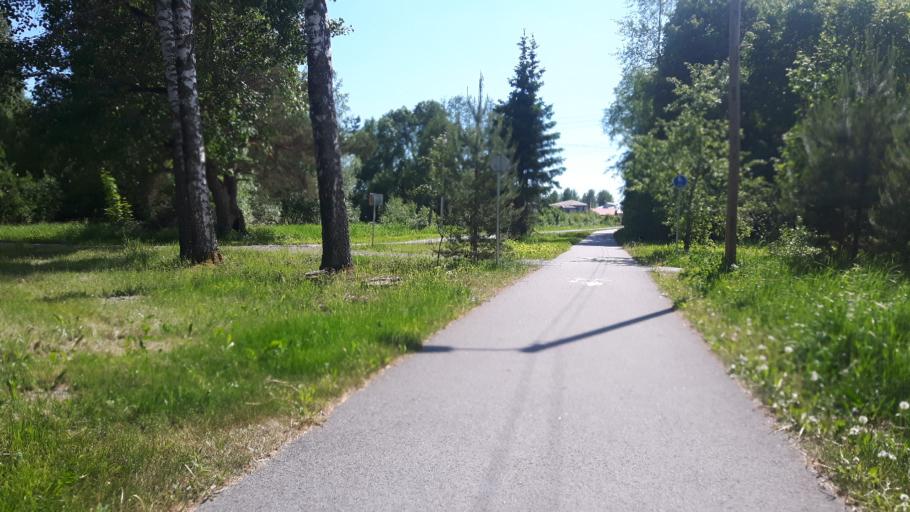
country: EE
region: Paernumaa
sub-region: Paikuse vald
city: Paikuse
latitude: 58.3914
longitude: 24.6410
